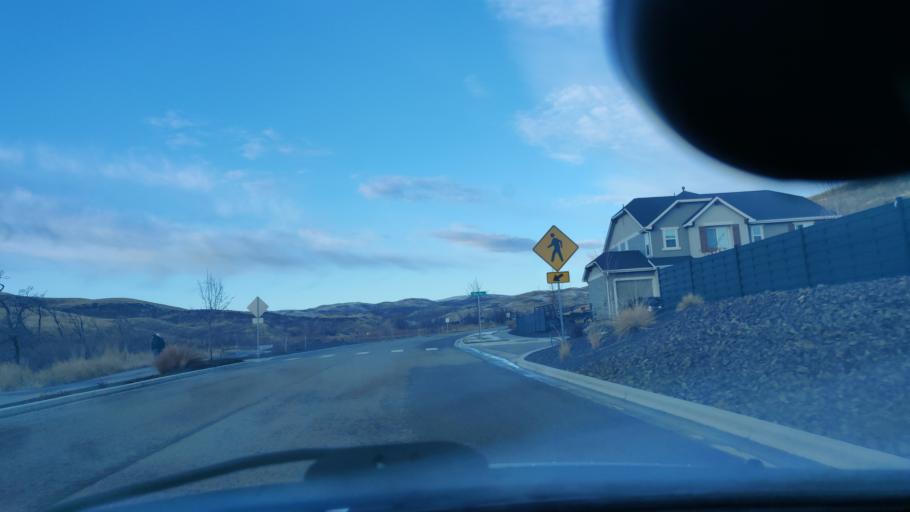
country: US
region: Idaho
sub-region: Ada County
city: Eagle
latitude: 43.7804
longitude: -116.2624
